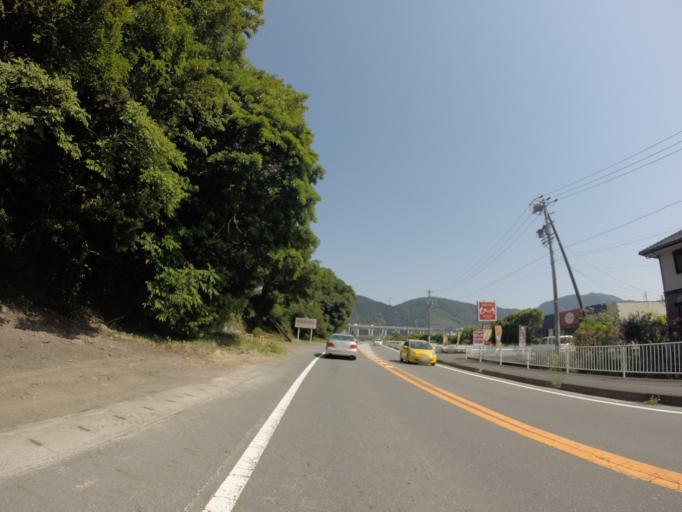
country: JP
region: Shizuoka
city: Fujinomiya
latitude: 35.1863
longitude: 138.6009
